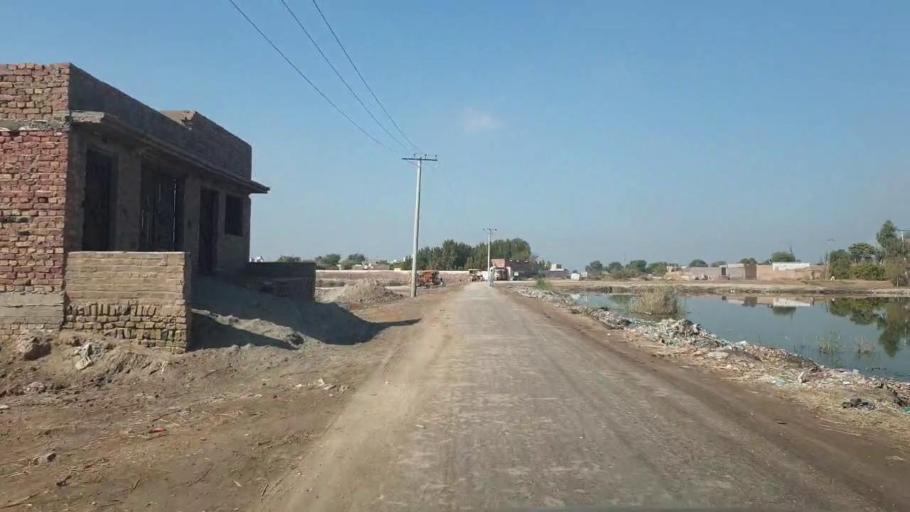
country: PK
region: Sindh
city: Shahdadpur
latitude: 25.9058
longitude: 68.5967
